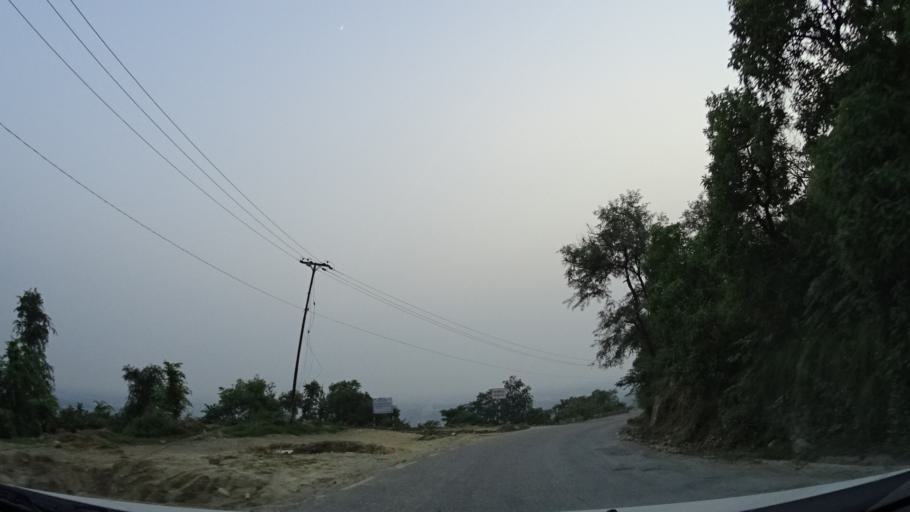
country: IN
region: Uttar Pradesh
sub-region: Maharajganj
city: Nichlaul
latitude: 27.5514
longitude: 83.8113
